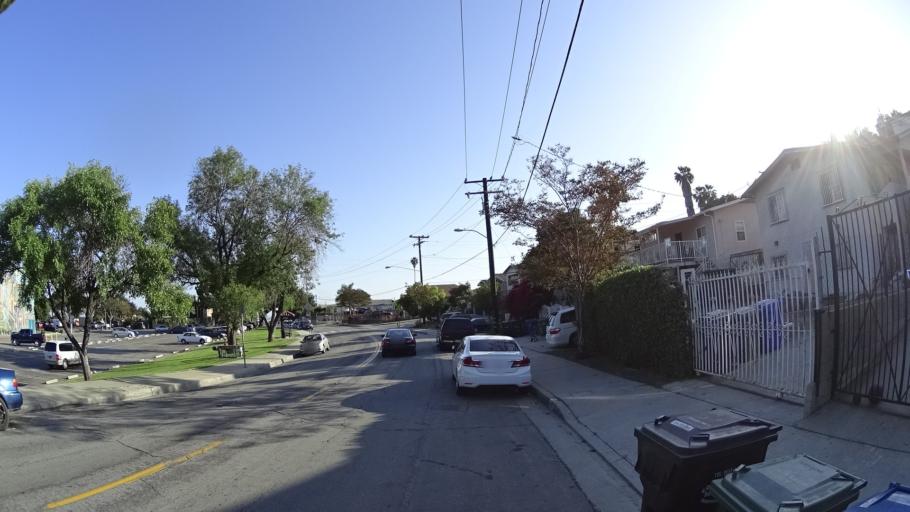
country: US
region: California
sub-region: Los Angeles County
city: Belvedere
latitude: 34.0489
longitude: -118.1799
